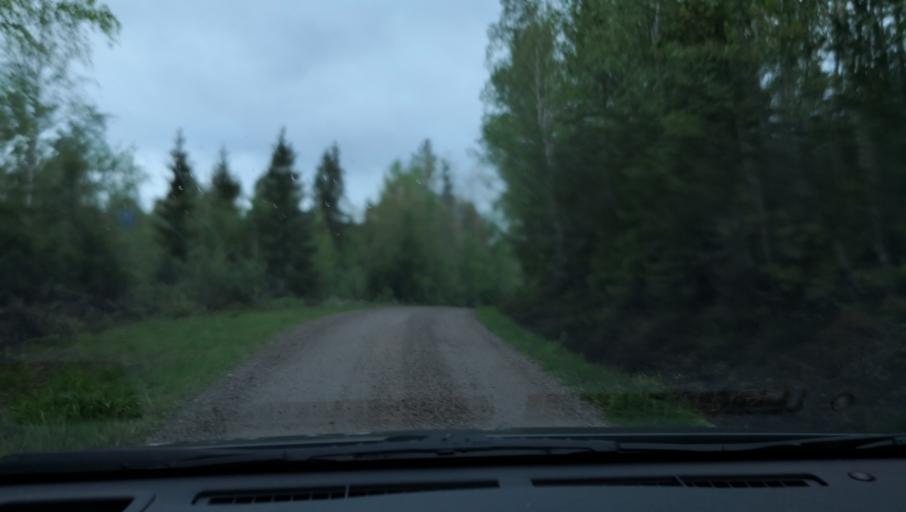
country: SE
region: Uppsala
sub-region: Heby Kommun
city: OEstervala
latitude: 59.9908
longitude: 17.2534
